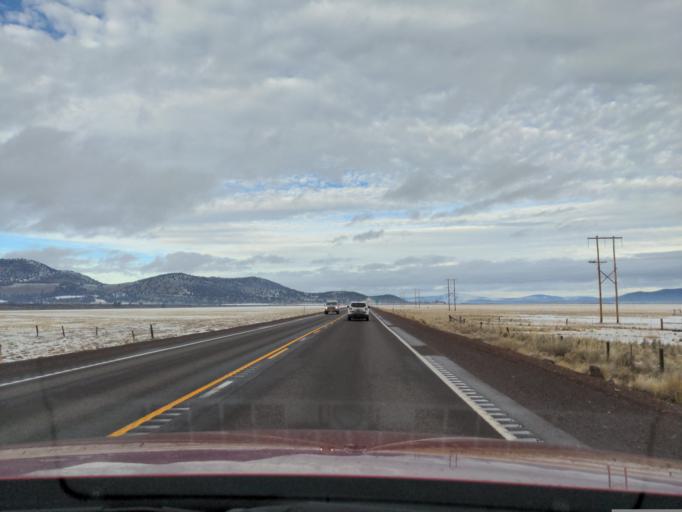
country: US
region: Oregon
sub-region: Klamath County
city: Klamath Falls
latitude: 42.0114
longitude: -121.8863
